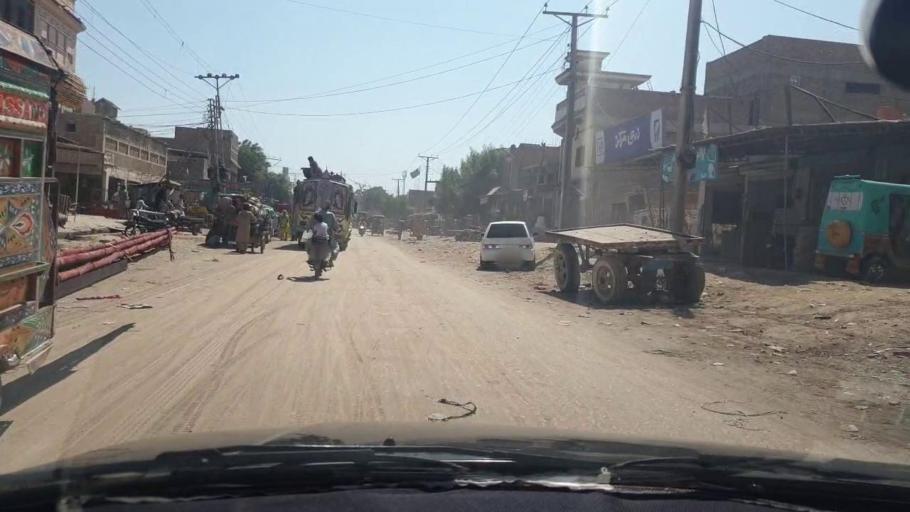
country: PK
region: Sindh
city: Tando Allahyar
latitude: 25.4547
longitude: 68.7218
